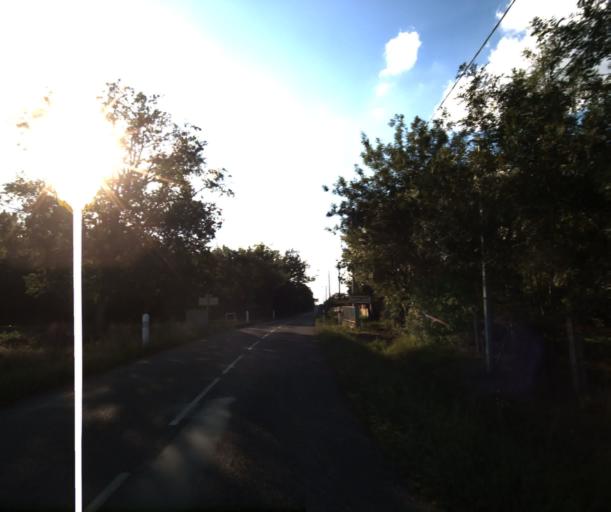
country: FR
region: Midi-Pyrenees
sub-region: Departement de la Haute-Garonne
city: Labastidette
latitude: 43.4790
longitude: 1.2511
